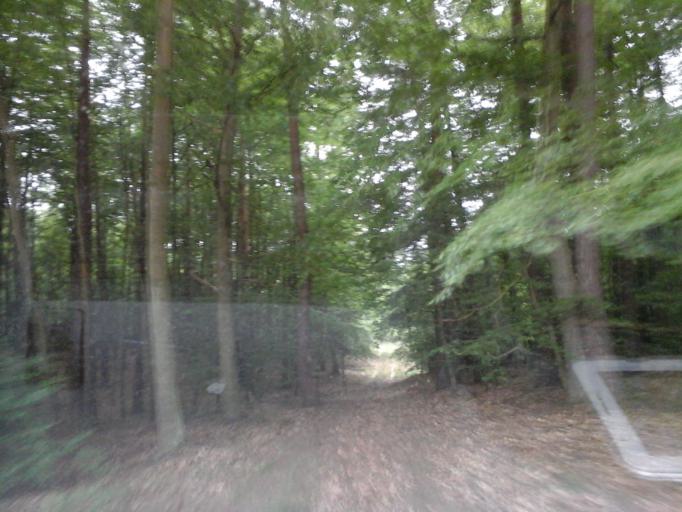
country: PL
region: West Pomeranian Voivodeship
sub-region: Powiat choszczenski
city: Pelczyce
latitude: 52.9595
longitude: 15.3761
